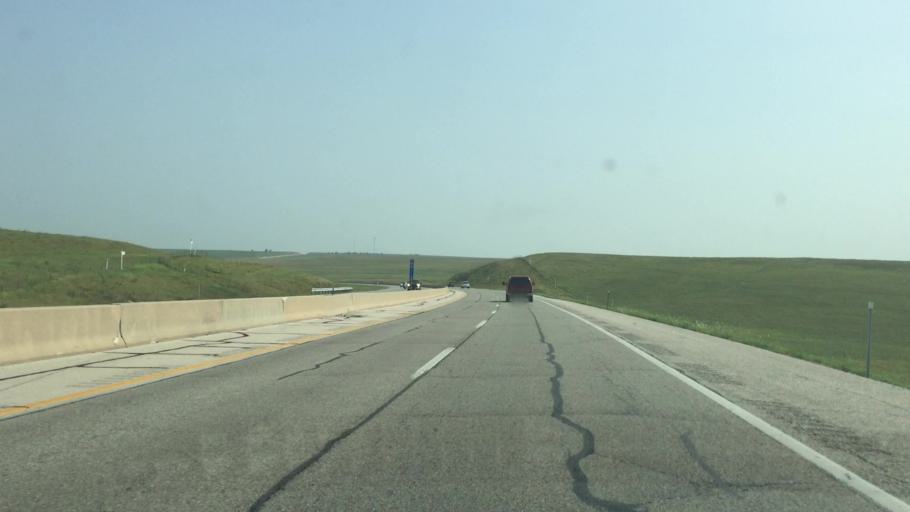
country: US
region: Kansas
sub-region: Chase County
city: Cottonwood Falls
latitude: 38.2362
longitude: -96.3984
